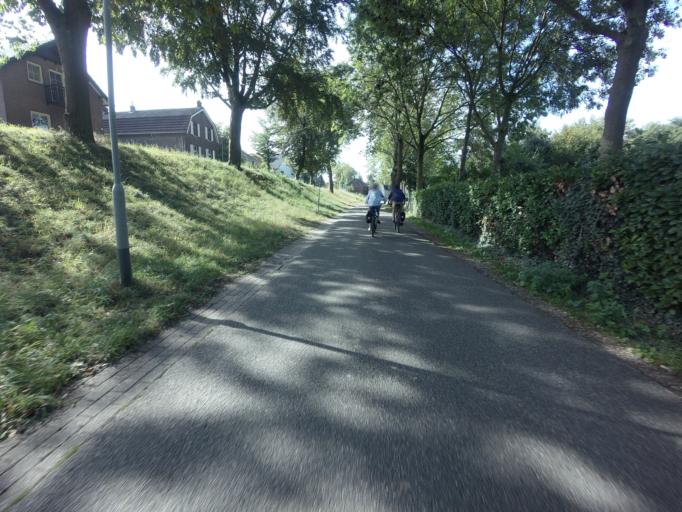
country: NL
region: Limburg
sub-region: Gemeente Roerdalen
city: Montfort
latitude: 51.1577
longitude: 5.9354
